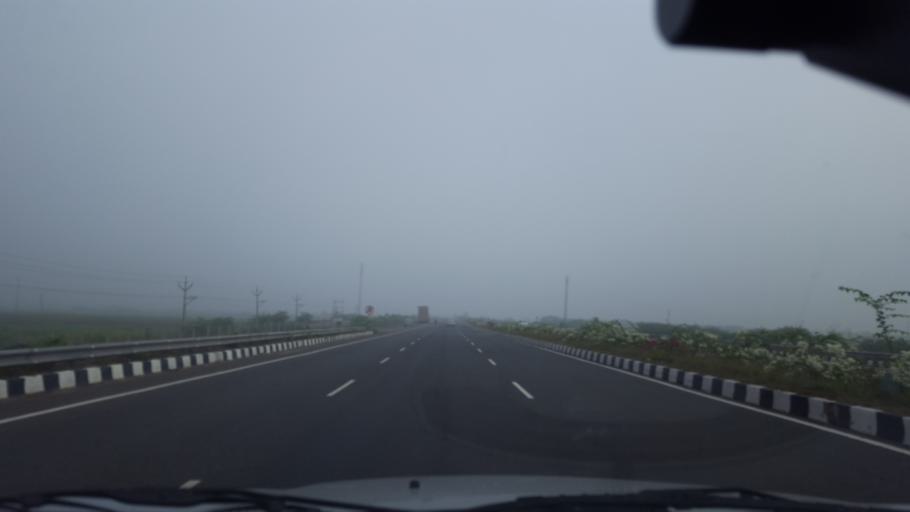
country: IN
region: Andhra Pradesh
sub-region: Prakasam
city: Ongole
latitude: 15.4790
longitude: 80.0604
